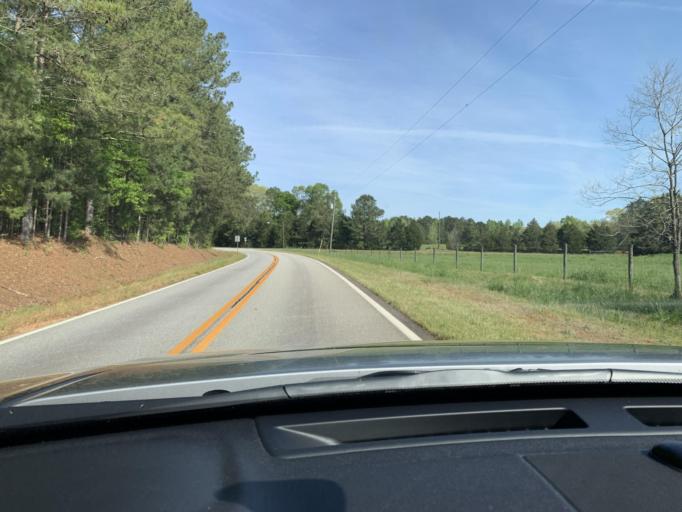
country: US
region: Georgia
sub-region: Oconee County
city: Watkinsville
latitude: 33.8152
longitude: -83.3170
